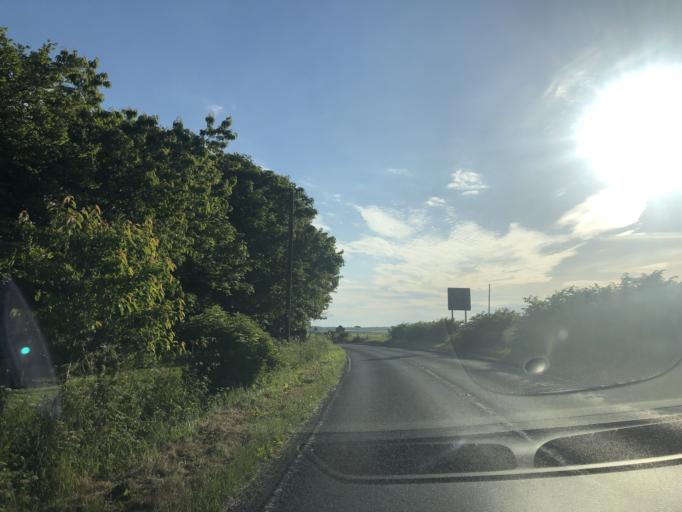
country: GB
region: Scotland
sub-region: Fife
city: Saint Monance
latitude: 56.2079
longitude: -2.7705
